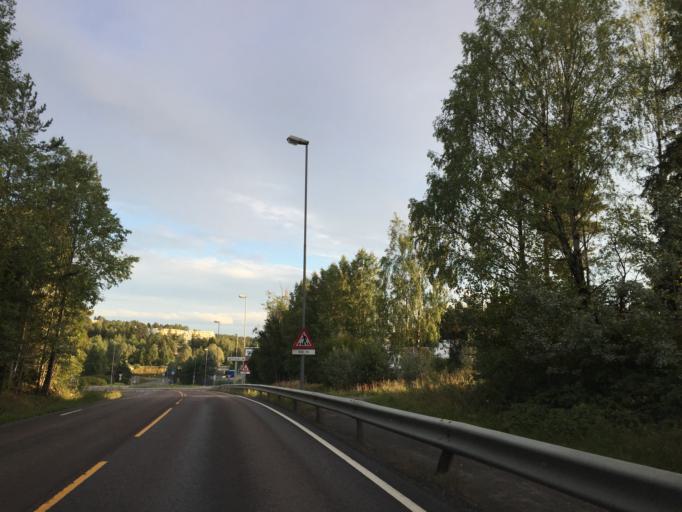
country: NO
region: Akershus
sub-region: Ski
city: Ski
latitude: 59.7650
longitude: 10.8428
